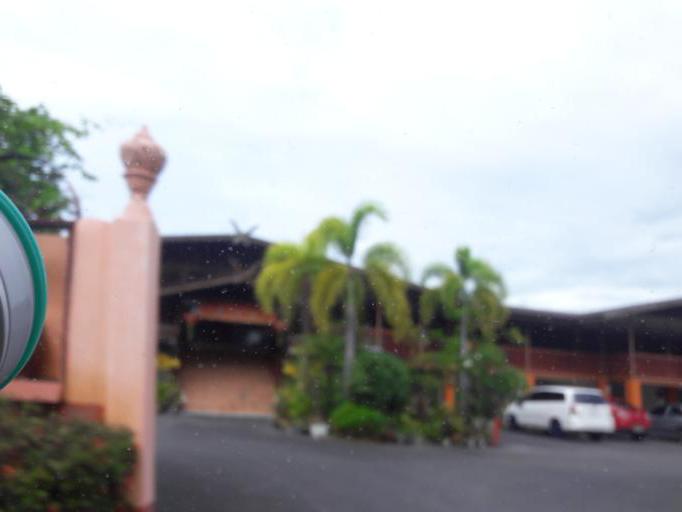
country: TH
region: Ratchaburi
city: Damnoen Saduak
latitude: 13.5230
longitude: 99.9742
